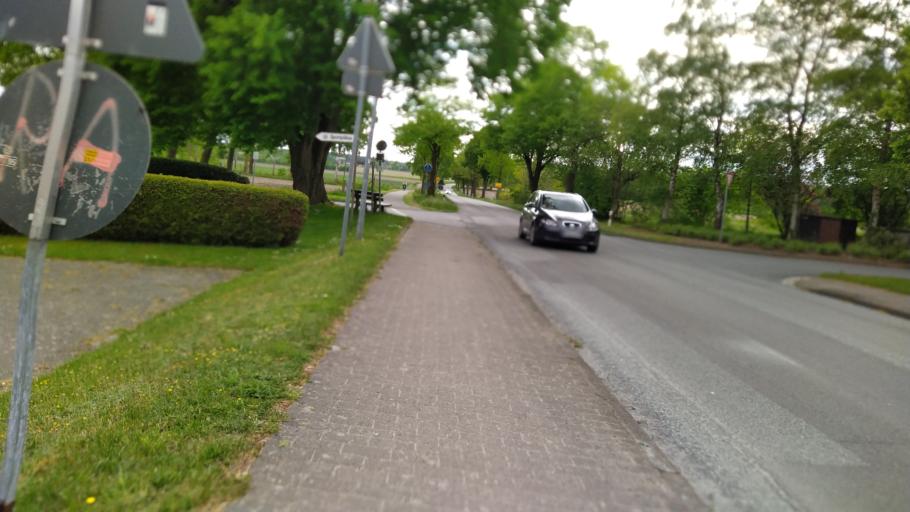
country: DE
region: Lower Saxony
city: Kirchtimke
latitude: 53.2489
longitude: 9.1485
